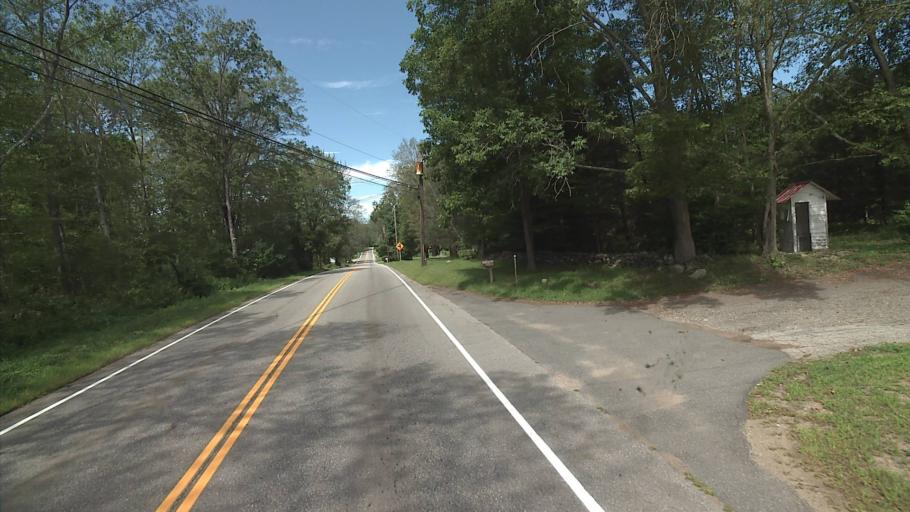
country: US
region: Connecticut
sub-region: Tolland County
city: Mansfield City
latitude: 41.7735
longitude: -72.2063
